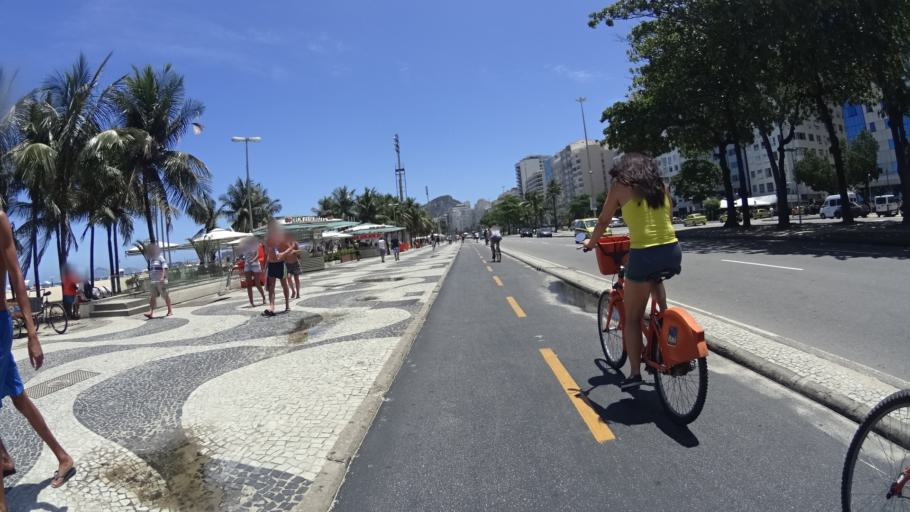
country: BR
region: Rio de Janeiro
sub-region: Rio De Janeiro
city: Rio de Janeiro
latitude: -22.9682
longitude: -43.1789
